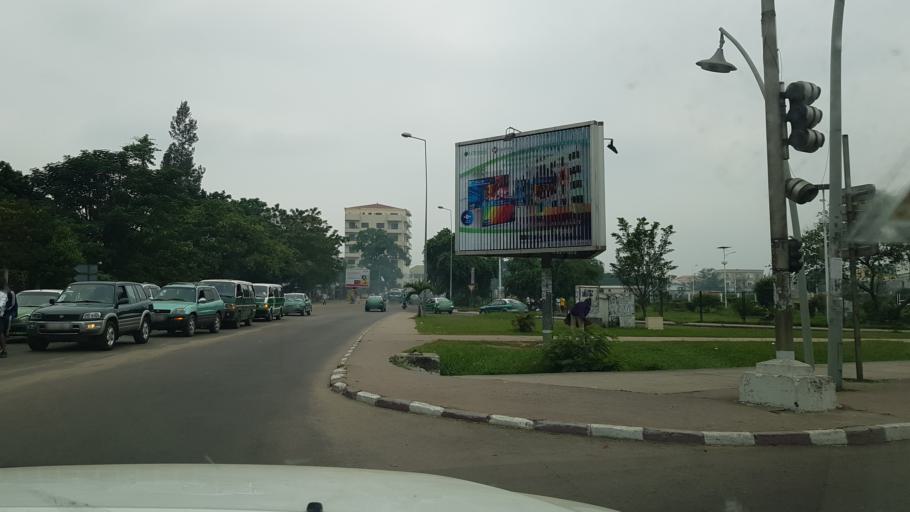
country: CG
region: Brazzaville
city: Brazzaville
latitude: -4.2642
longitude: 15.2610
